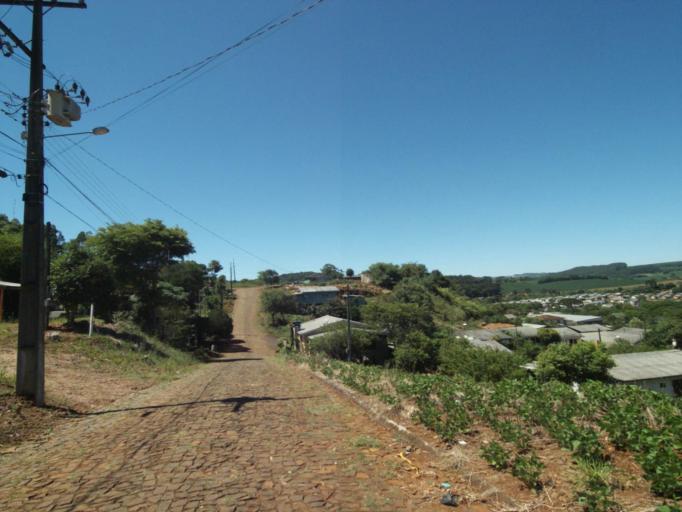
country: BR
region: Parana
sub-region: Pato Branco
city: Pato Branco
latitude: -26.2685
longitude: -52.7745
